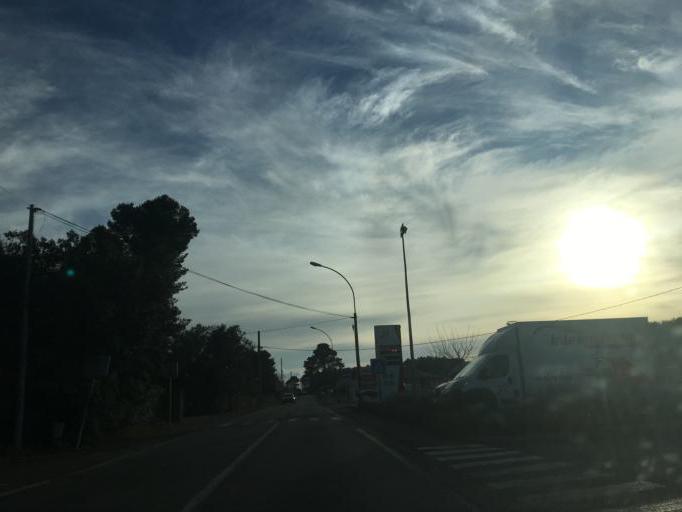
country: FR
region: Provence-Alpes-Cote d'Azur
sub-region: Departement du Var
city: Aups
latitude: 43.6169
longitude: 6.2200
